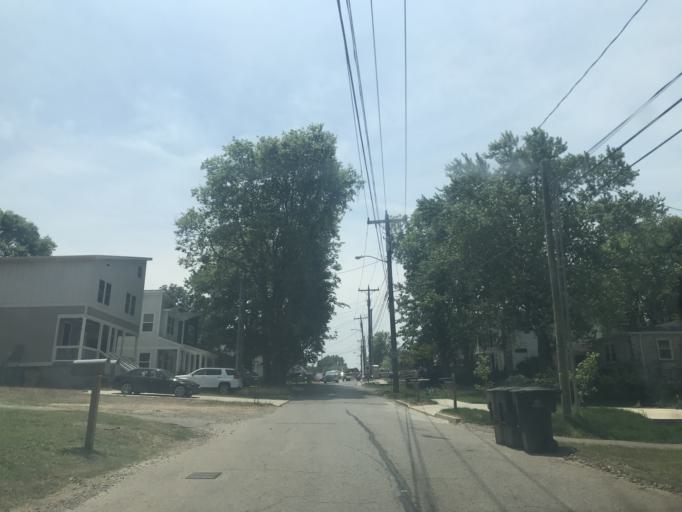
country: US
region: Tennessee
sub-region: Davidson County
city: Nashville
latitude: 36.1909
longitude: -86.8151
